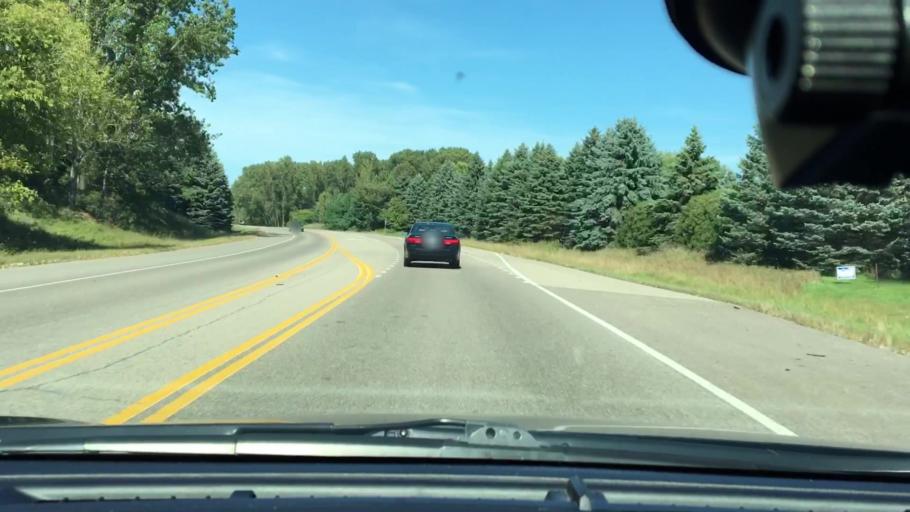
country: US
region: Minnesota
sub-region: Washington County
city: Mahtomedi
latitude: 45.0495
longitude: -92.9479
